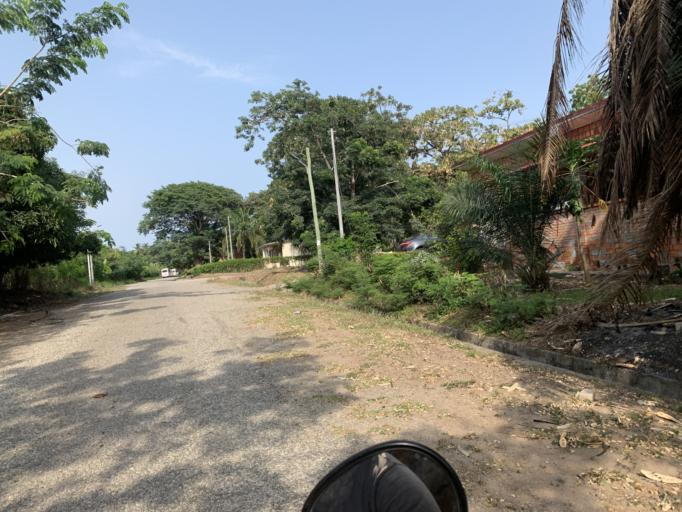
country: GH
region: Central
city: Winneba
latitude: 5.3389
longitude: -0.6298
